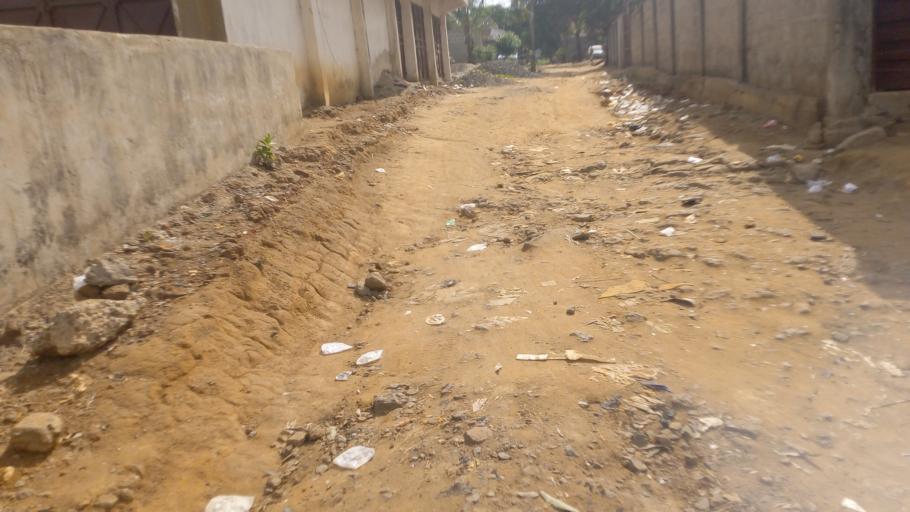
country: SL
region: Western Area
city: Waterloo
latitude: 8.3223
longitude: -13.0727
